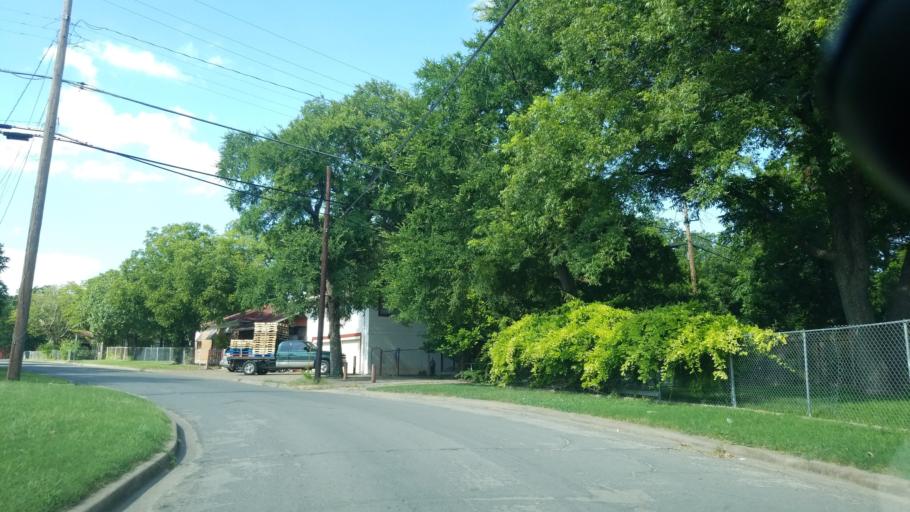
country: US
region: Texas
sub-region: Dallas County
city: Balch Springs
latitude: 32.7675
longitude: -96.7053
